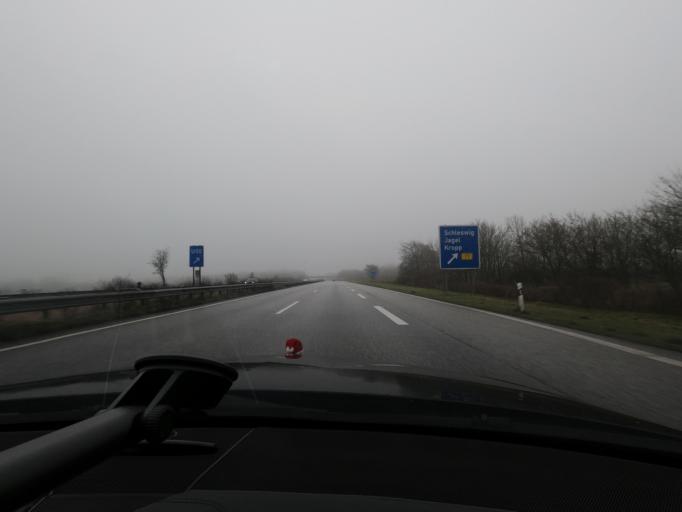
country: DE
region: Schleswig-Holstein
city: Busdorf
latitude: 54.4860
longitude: 9.5297
